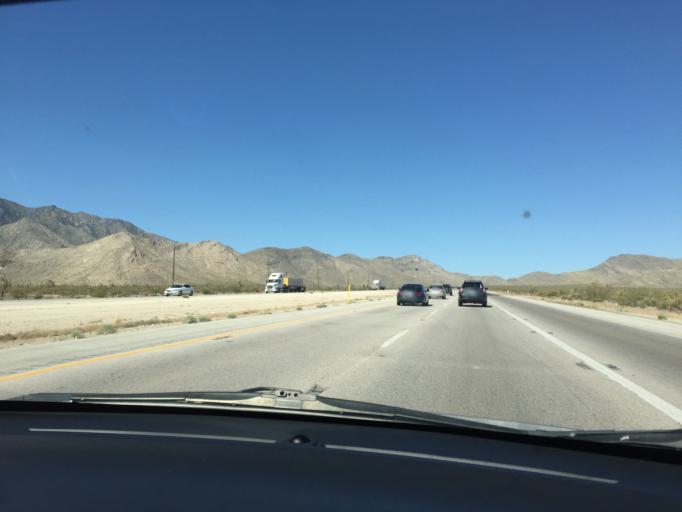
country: US
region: Nevada
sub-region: Clark County
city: Sandy Valley
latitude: 35.4627
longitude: -115.6208
